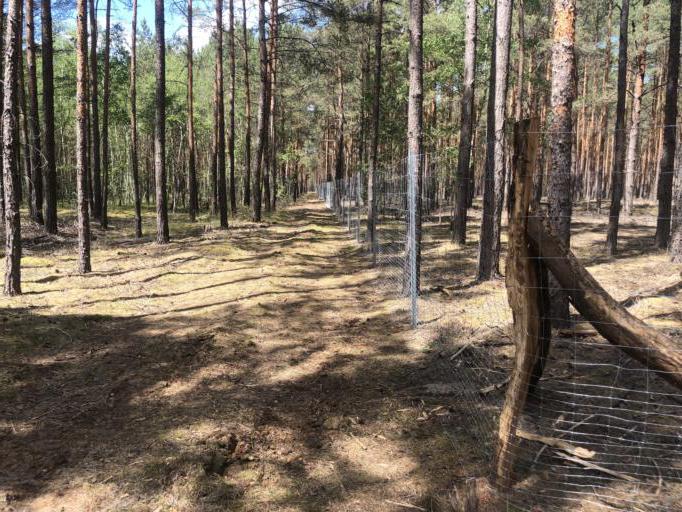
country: DE
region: Brandenburg
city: Gross Koris
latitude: 52.1885
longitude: 13.6412
